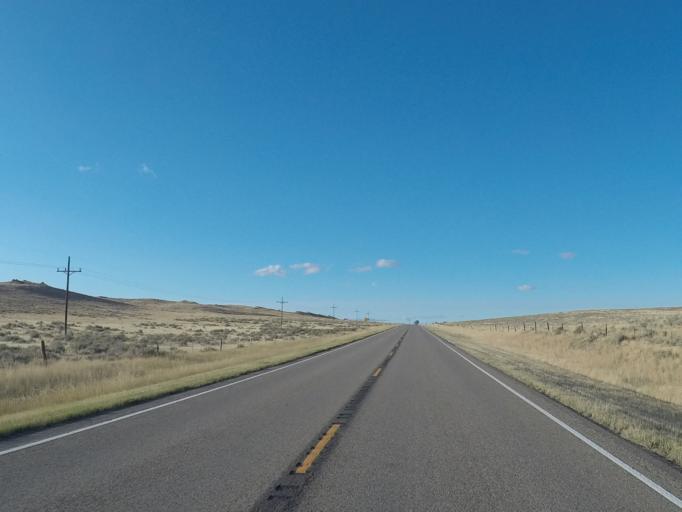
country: US
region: Montana
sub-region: Golden Valley County
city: Ryegate
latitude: 46.2367
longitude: -108.9343
